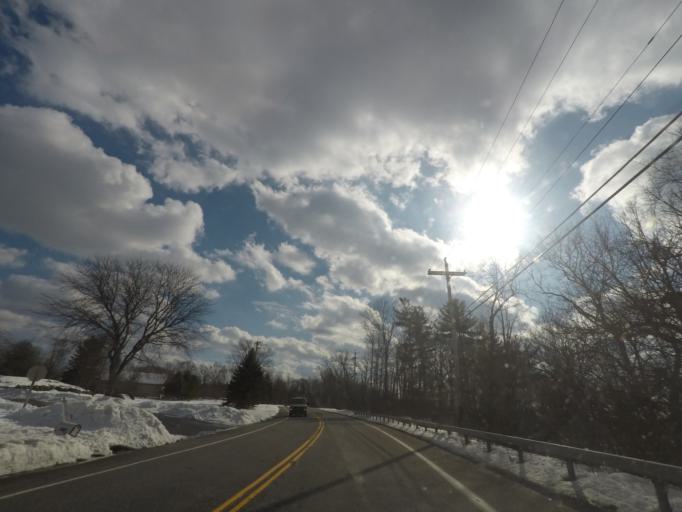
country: US
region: New York
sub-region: Schenectady County
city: East Glenville
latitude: 42.8472
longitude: -73.8771
